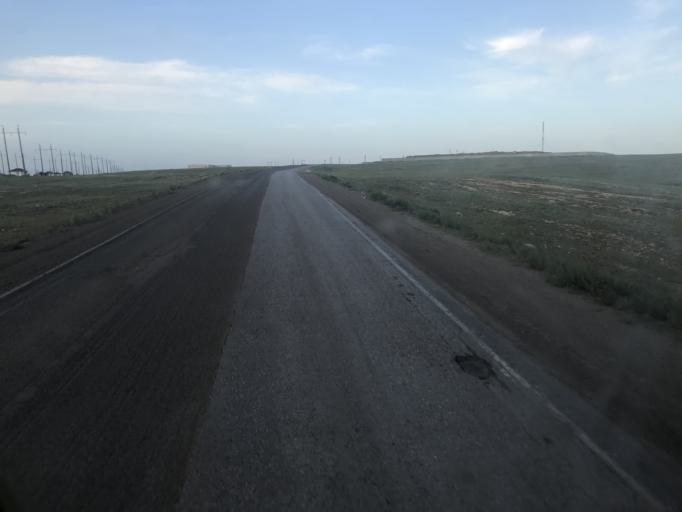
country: KZ
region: Aqtoebe
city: Khromtau
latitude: 50.2585
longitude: 58.3971
